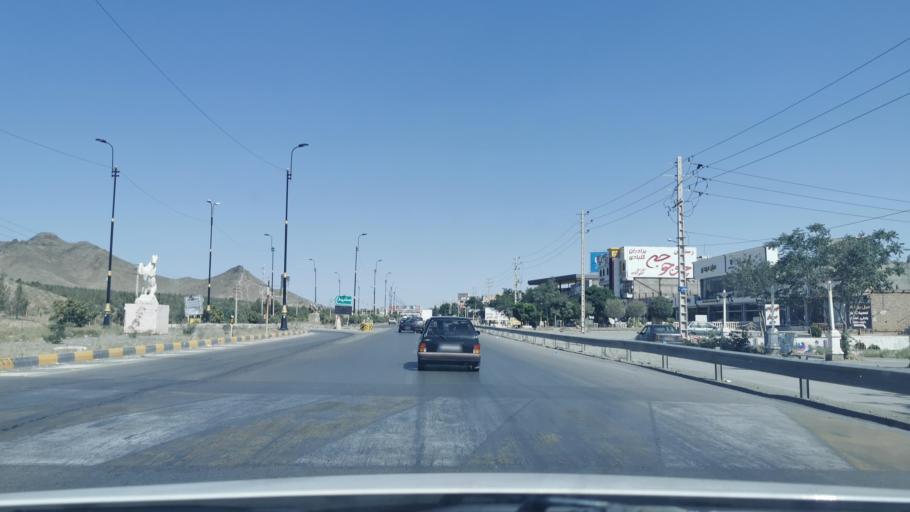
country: IR
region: Razavi Khorasan
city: Torqabeh
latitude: 36.3892
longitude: 59.4075
